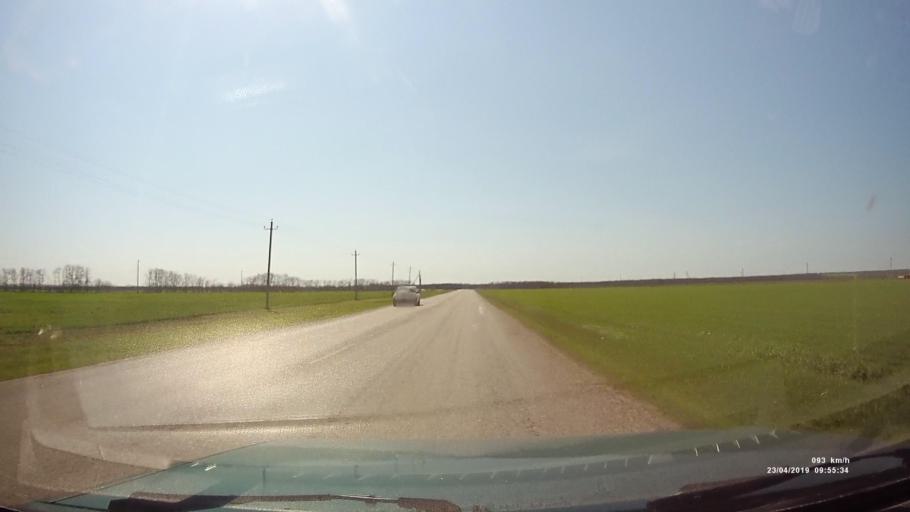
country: RU
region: Rostov
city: Orlovskiy
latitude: 46.8072
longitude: 42.0637
